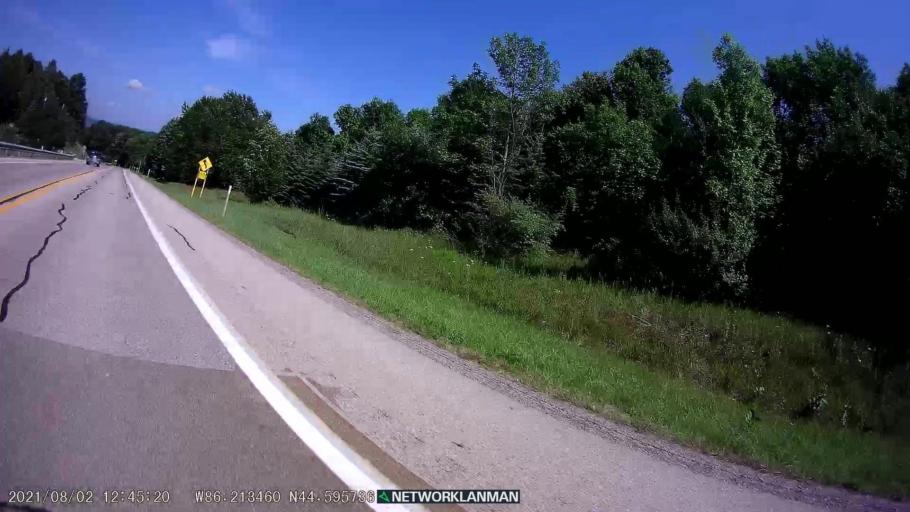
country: US
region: Michigan
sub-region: Benzie County
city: Frankfort
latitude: 44.5960
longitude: -86.2129
